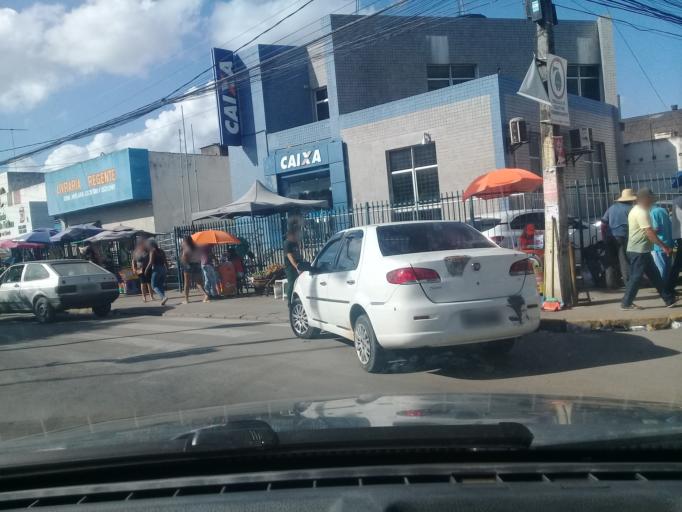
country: BR
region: Pernambuco
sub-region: Vitoria De Santo Antao
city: Vitoria de Santo Antao
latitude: -8.1201
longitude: -35.2958
